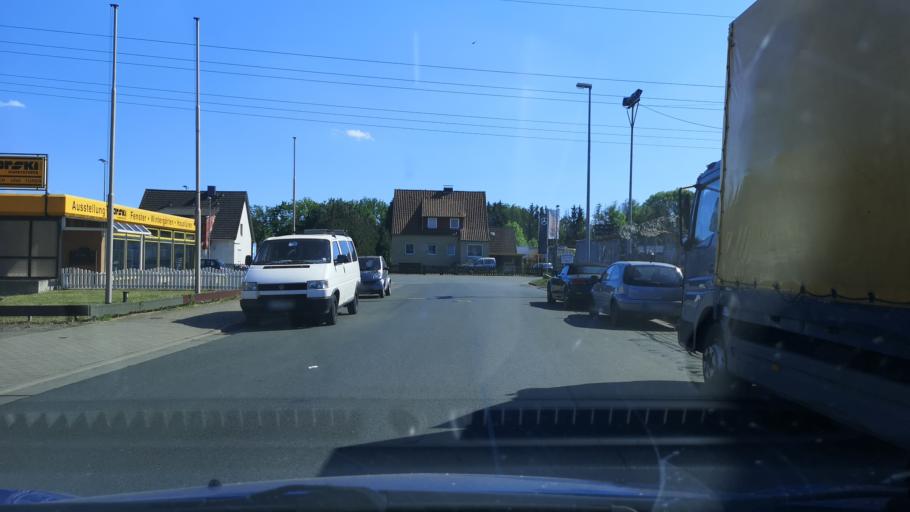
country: DE
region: Lower Saxony
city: Langenhagen
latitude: 52.4321
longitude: 9.6873
